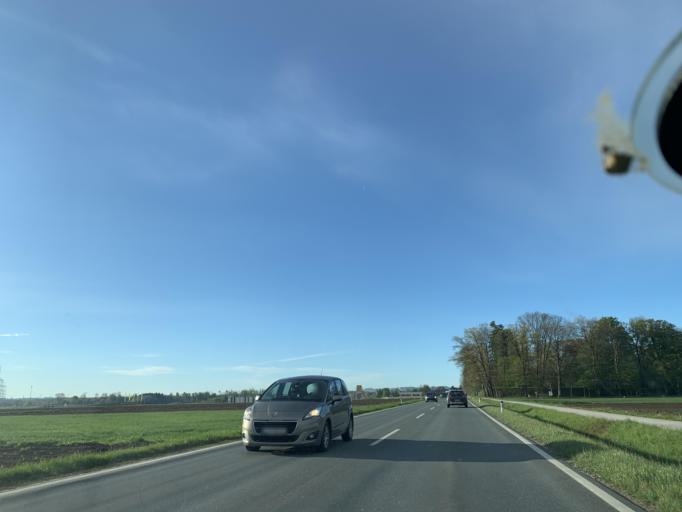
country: AT
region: Styria
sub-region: Politischer Bezirk Leibnitz
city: Lang
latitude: 46.8476
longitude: 15.5160
